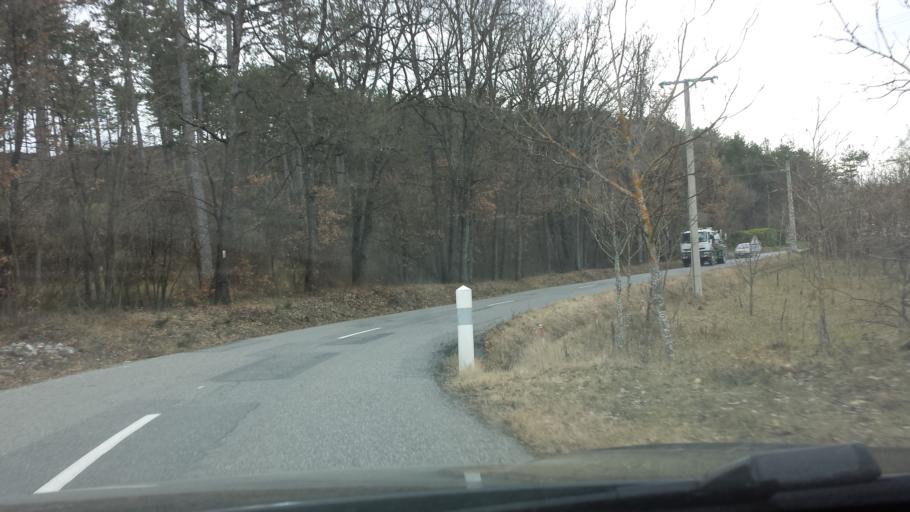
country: FR
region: Provence-Alpes-Cote d'Azur
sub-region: Departement des Alpes-de-Haute-Provence
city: Digne-les-Bains
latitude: 44.0634
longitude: 6.1820
